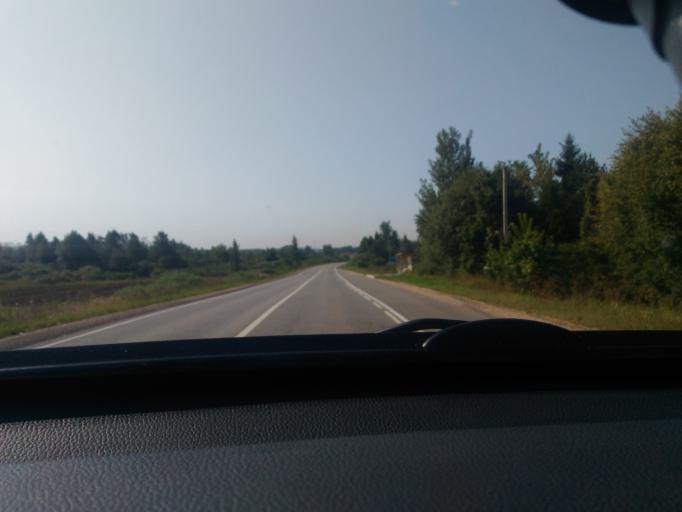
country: RU
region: Moskovskaya
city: Podosinki
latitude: 56.2319
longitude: 37.5499
